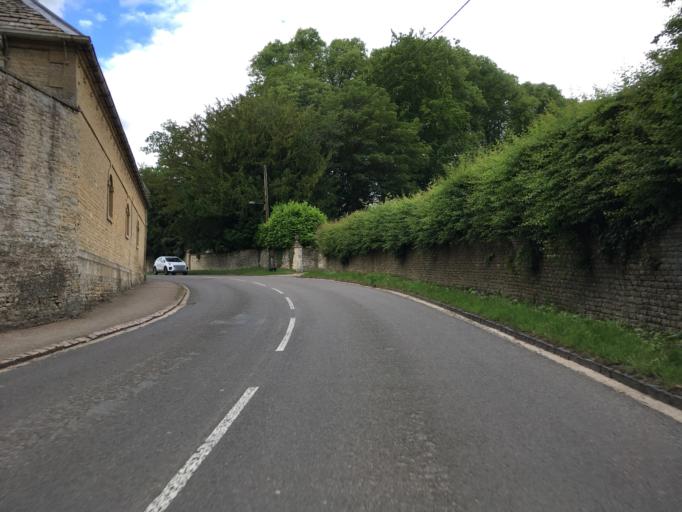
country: GB
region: England
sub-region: Oxfordshire
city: Shipton under Wychwood
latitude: 51.8563
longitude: -1.5990
